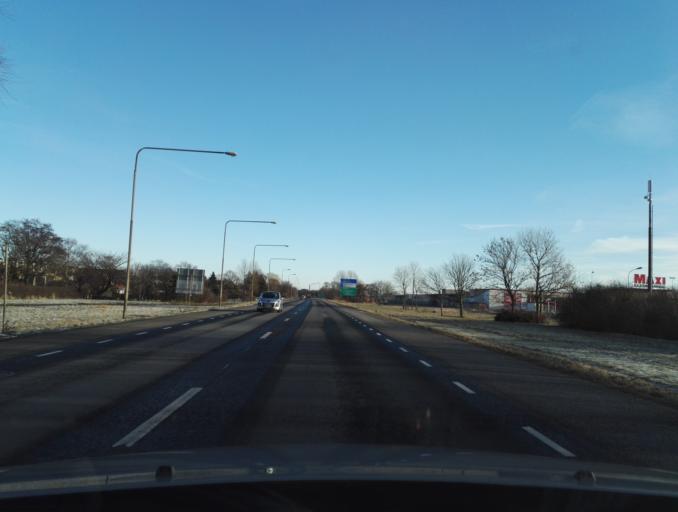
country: SE
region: Skane
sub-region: Trelleborgs Kommun
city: Trelleborg
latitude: 55.3753
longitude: 13.1275
